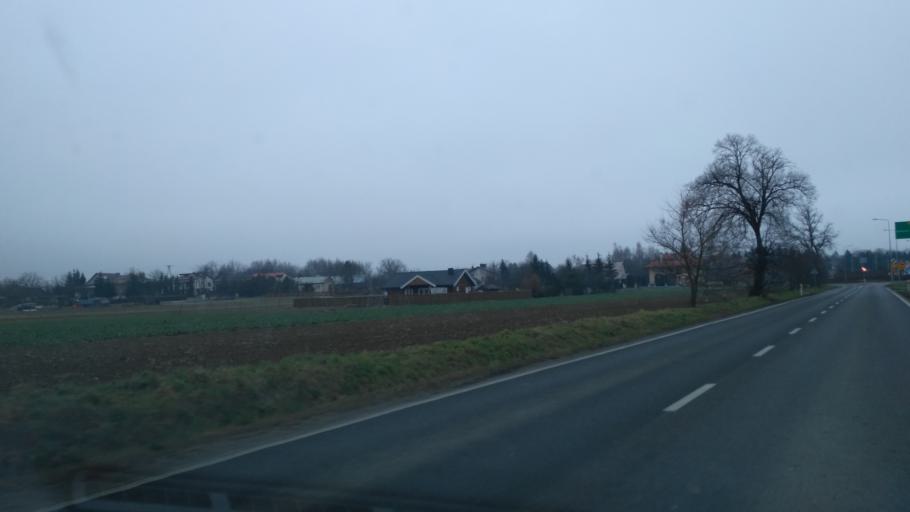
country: PL
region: Subcarpathian Voivodeship
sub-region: Powiat jaroslawski
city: Pawlosiow
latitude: 49.9762
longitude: 22.6397
